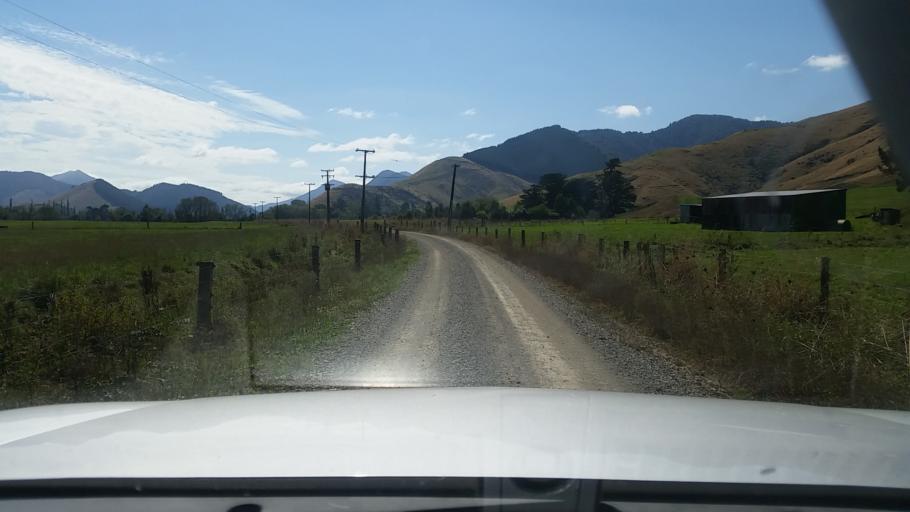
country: NZ
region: Nelson
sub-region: Nelson City
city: Nelson
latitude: -41.2599
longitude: 173.5811
